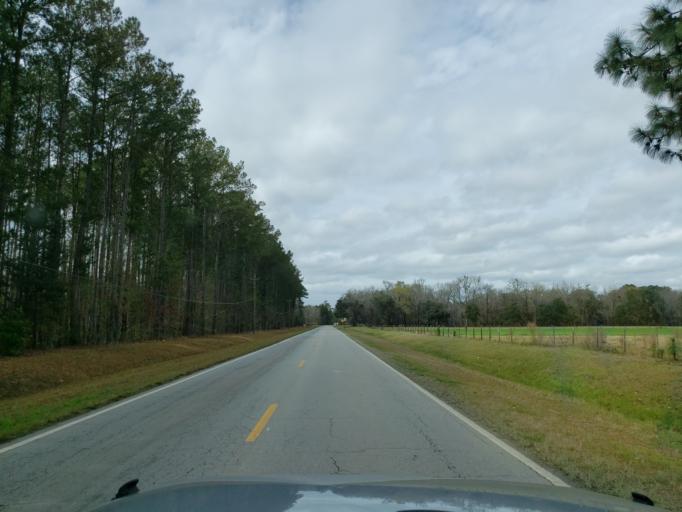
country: US
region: Georgia
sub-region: Chatham County
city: Georgetown
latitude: 32.0399
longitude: -81.2767
